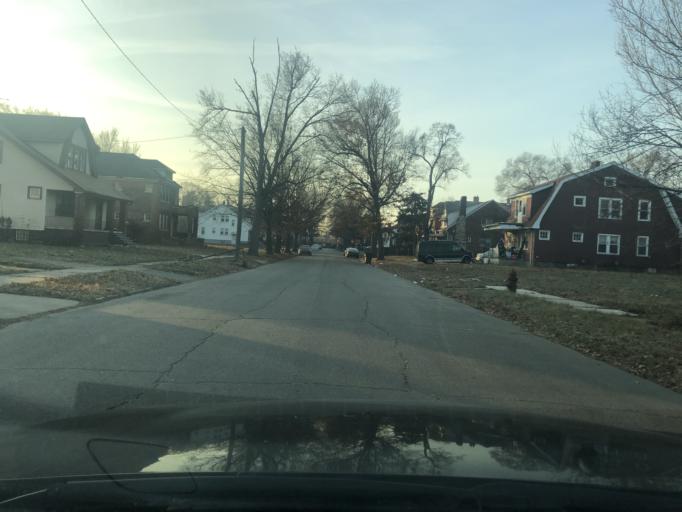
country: US
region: Michigan
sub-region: Wayne County
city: Highland Park
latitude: 42.3999
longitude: -83.1367
